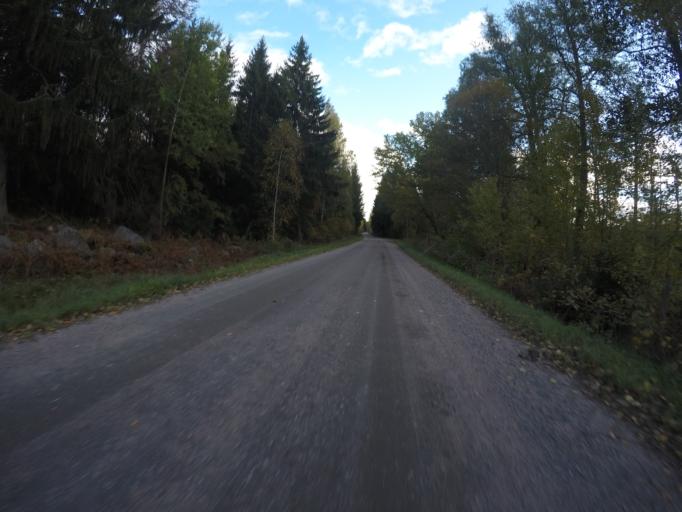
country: SE
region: Vaestmanland
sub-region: Arboga Kommun
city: Tyringe
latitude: 59.3346
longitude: 15.9657
